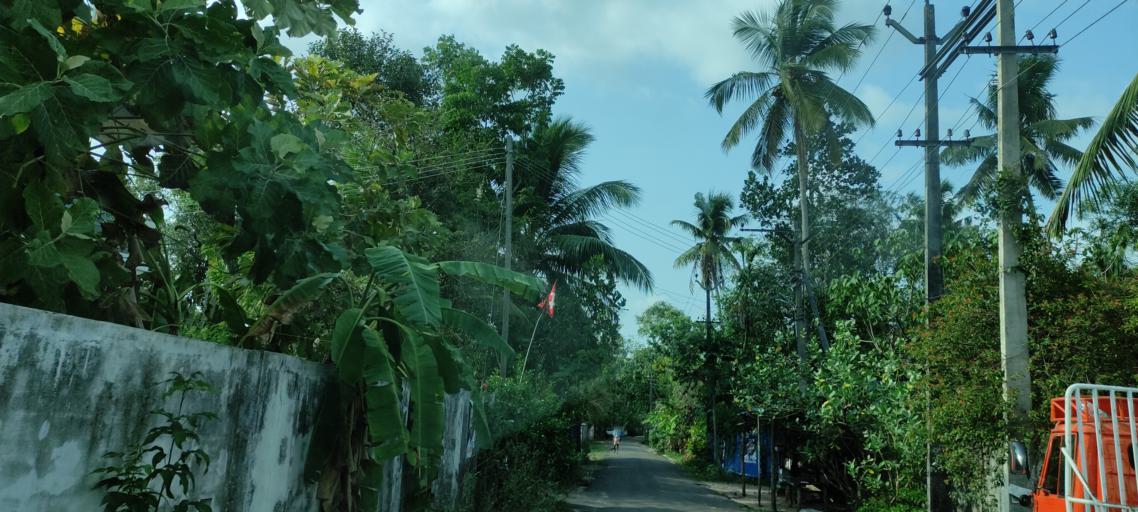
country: IN
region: Kerala
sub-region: Alappuzha
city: Vayalar
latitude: 9.6835
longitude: 76.3254
